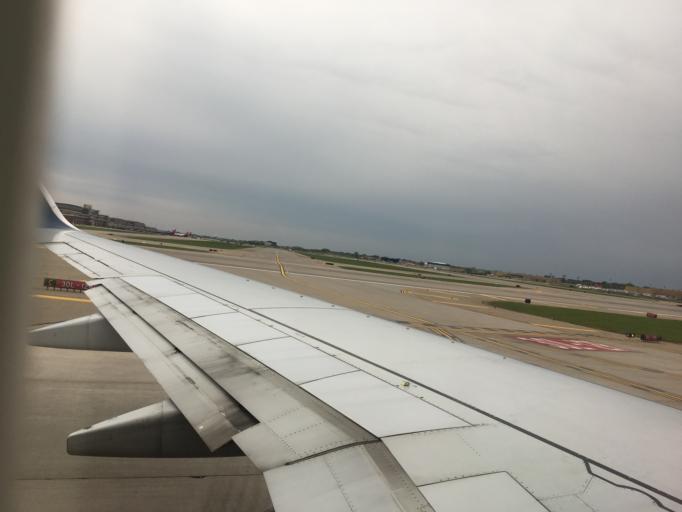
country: US
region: Minnesota
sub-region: Hennepin County
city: Richfield
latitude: 44.8832
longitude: -93.2204
